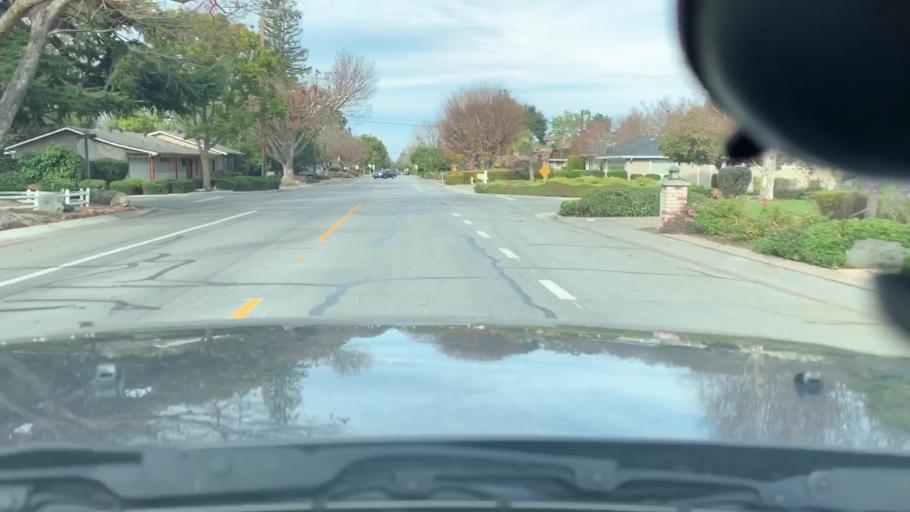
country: US
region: California
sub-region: Santa Clara County
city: Loyola
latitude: 37.3550
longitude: -122.0687
